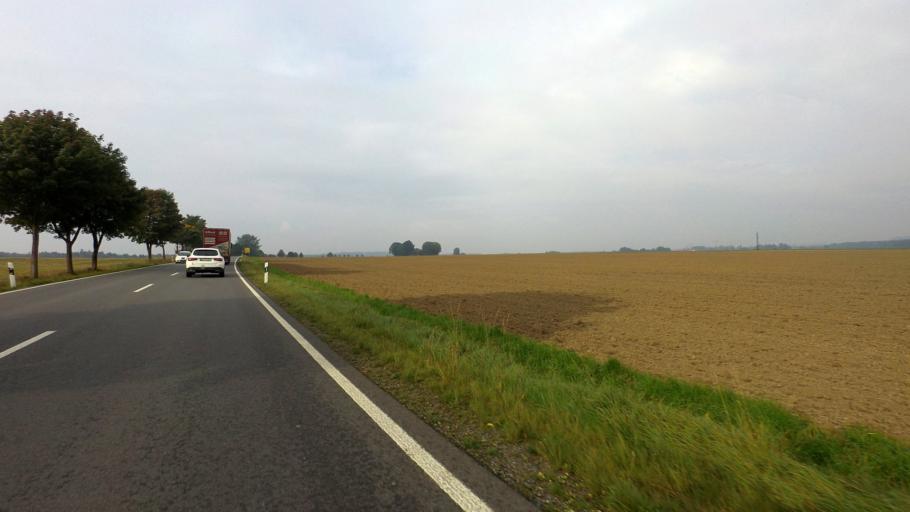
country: DE
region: Saxony
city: Stolpen
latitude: 51.0801
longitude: 14.0412
